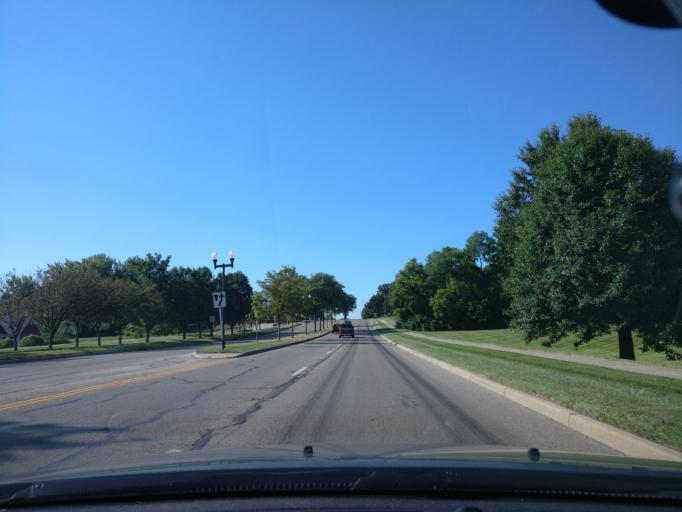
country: US
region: Ohio
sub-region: Montgomery County
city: Centerville
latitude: 39.6178
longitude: -84.1600
